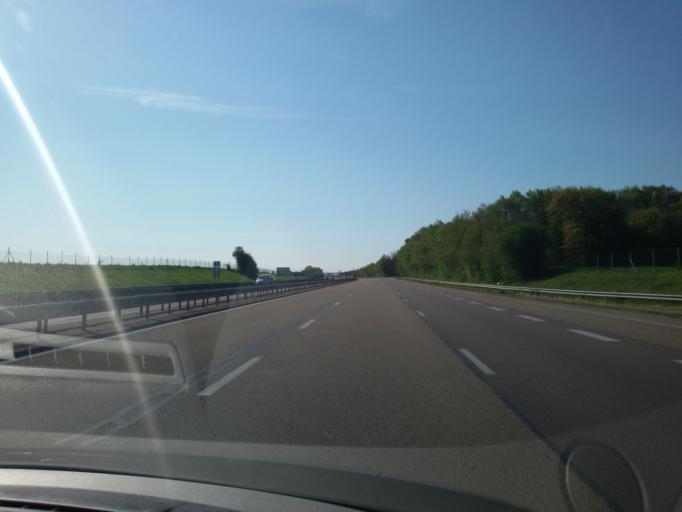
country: FR
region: Bourgogne
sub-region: Departement de l'Yonne
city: Saint-Julien-du-Sault
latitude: 47.9717
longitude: 3.2015
